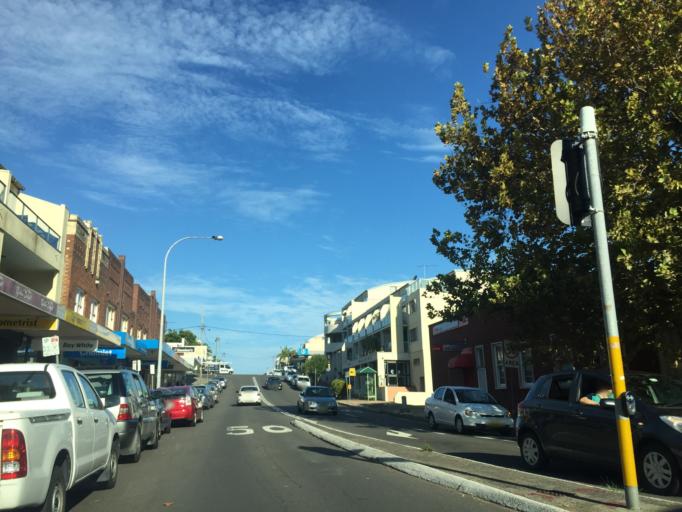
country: AU
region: New South Wales
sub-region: Warringah
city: Narrabeen
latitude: -33.7127
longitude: 151.2974
